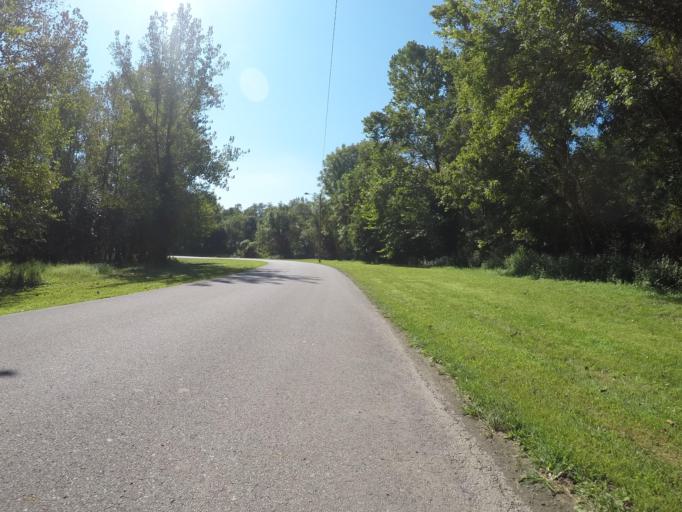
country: US
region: Kentucky
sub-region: Boyd County
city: Catlettsburg
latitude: 38.4106
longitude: -82.5938
